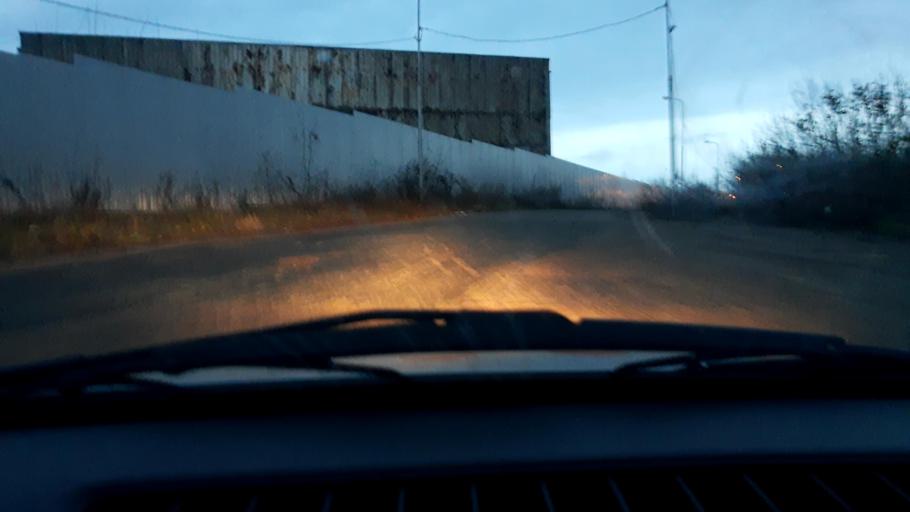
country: RU
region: Bashkortostan
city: Avdon
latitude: 54.6740
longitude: 55.8065
